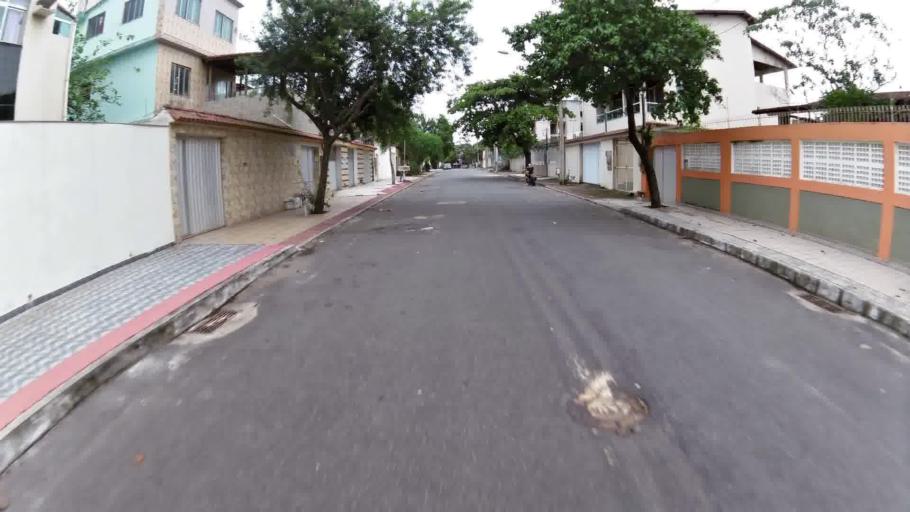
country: BR
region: Espirito Santo
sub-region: Guarapari
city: Guarapari
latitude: -20.6547
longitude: -40.4929
